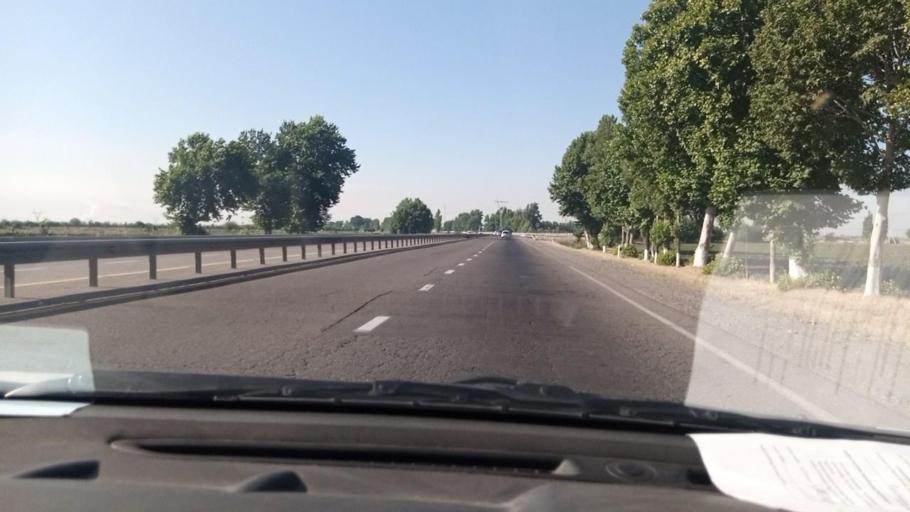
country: UZ
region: Toshkent Shahri
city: Bektemir
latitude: 41.1922
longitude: 69.4031
